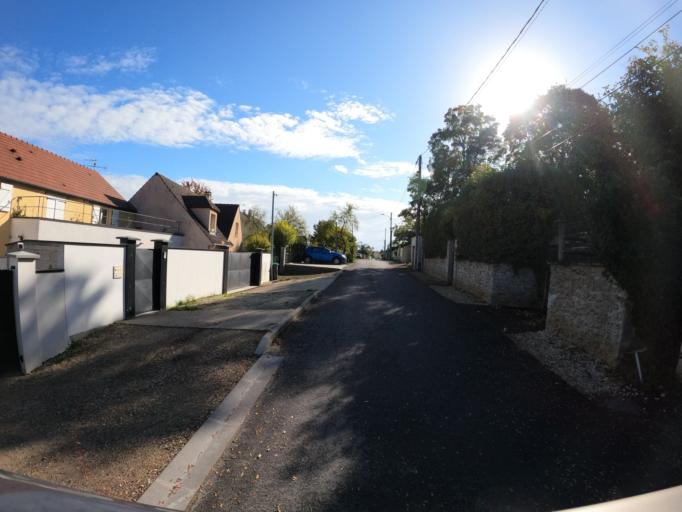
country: FR
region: Ile-de-France
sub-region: Departement de Seine-et-Marne
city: Montry
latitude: 48.8866
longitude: 2.8241
